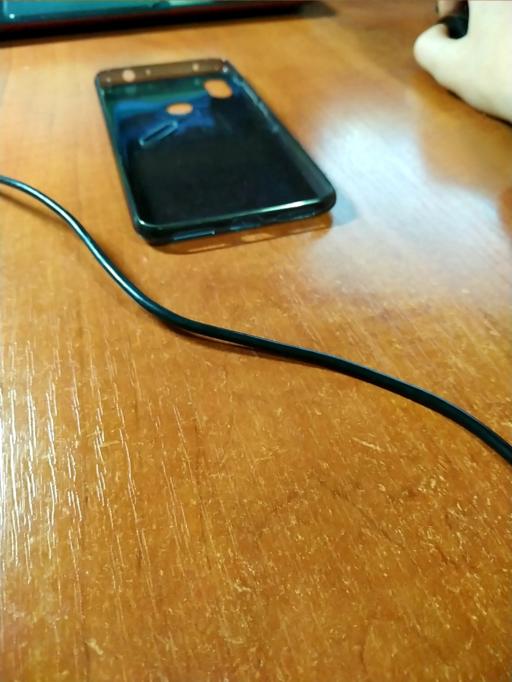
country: RU
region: Kaluga
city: Iznoski
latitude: 54.9874
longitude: 35.4102
